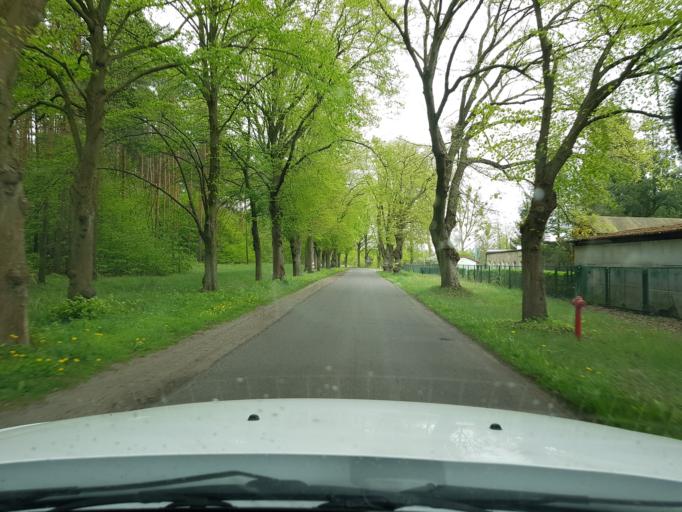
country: PL
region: West Pomeranian Voivodeship
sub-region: Powiat mysliborski
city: Debno
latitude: 52.6954
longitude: 14.6797
